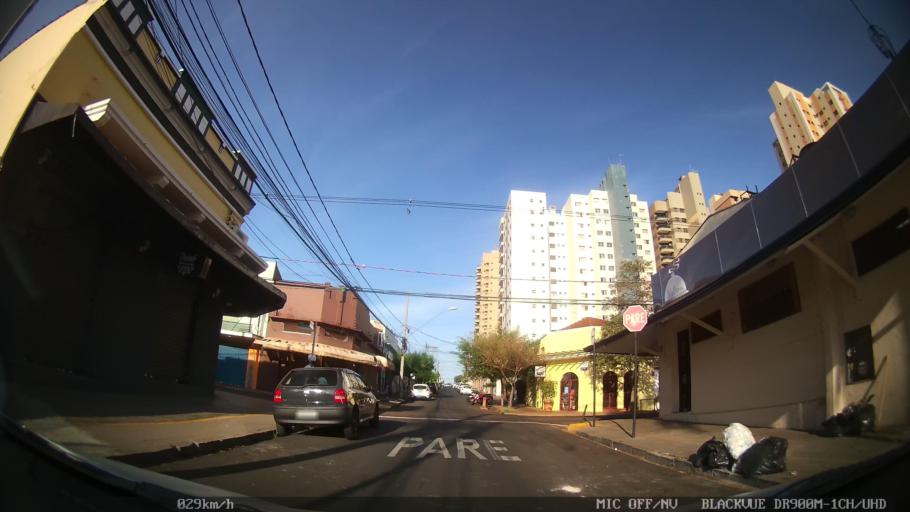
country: BR
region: Sao Paulo
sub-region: Ribeirao Preto
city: Ribeirao Preto
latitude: -21.1840
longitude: -47.8050
